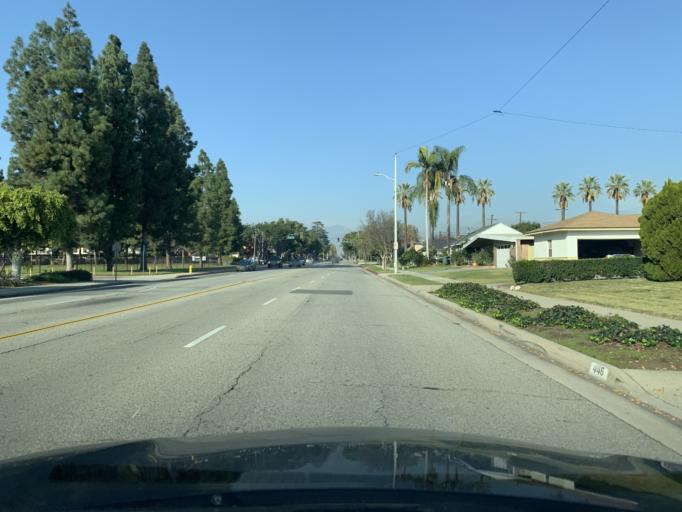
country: US
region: California
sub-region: Los Angeles County
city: Covina
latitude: 34.0815
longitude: -117.8989
